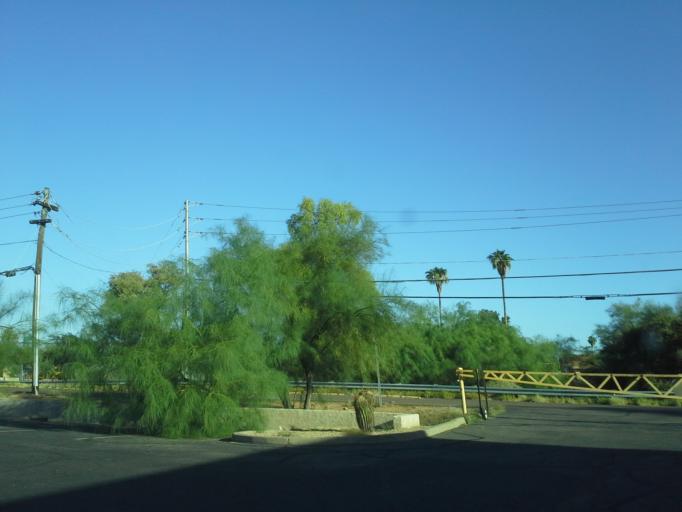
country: US
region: Arizona
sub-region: Maricopa County
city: Glendale
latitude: 33.6035
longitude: -112.0988
